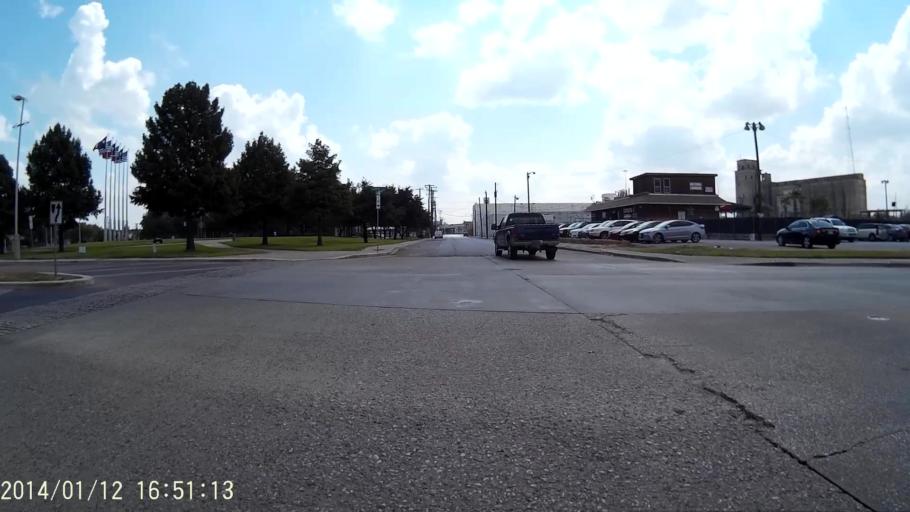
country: US
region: Texas
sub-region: Dallas County
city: Dallas
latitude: 32.7841
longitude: -96.7745
